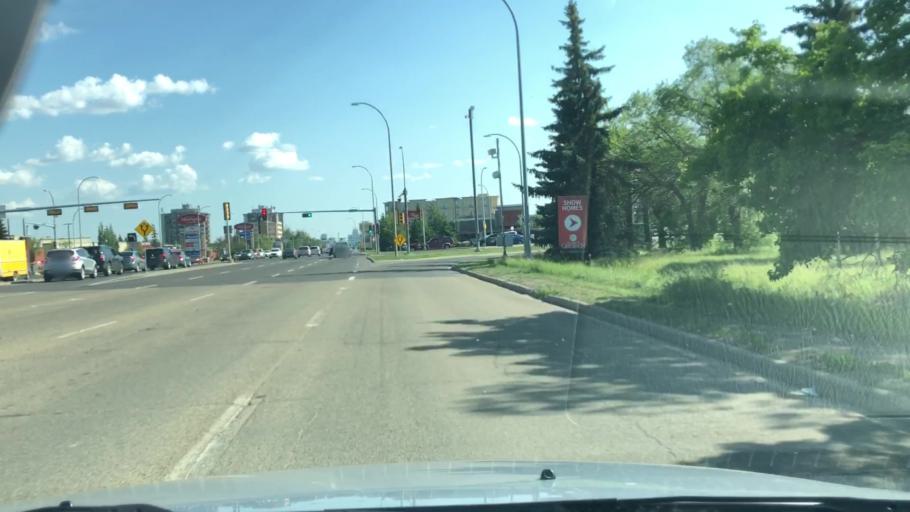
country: CA
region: Alberta
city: Edmonton
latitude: 53.6004
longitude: -113.4923
